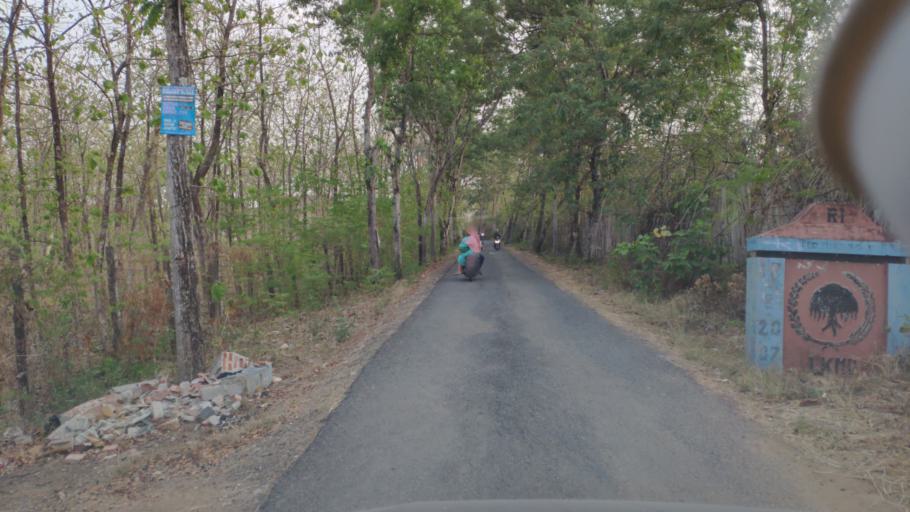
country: ID
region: Central Java
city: Tawangsari
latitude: -6.9748
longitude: 111.3504
